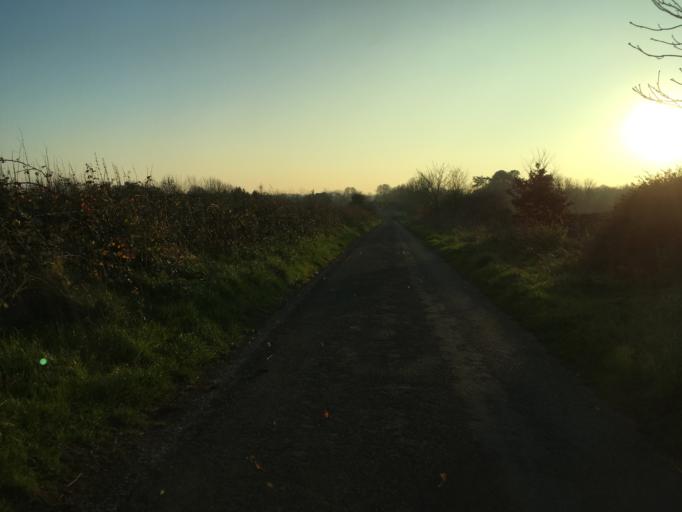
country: GB
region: England
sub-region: Wiltshire
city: Nettleton
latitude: 51.4707
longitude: -2.2831
